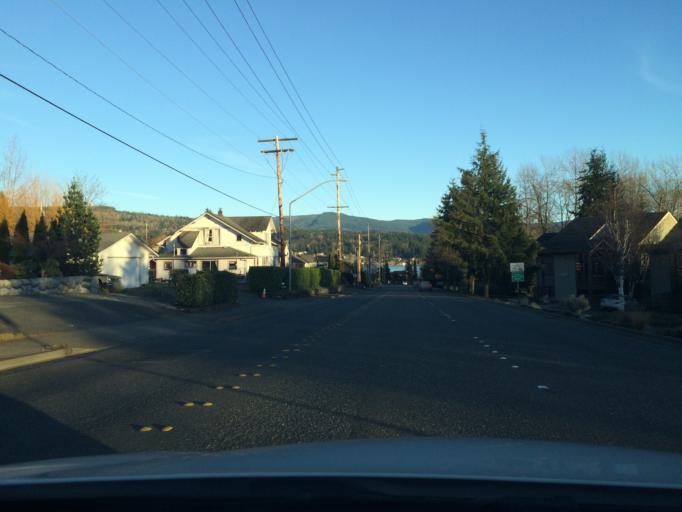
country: US
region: Washington
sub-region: Whatcom County
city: Geneva
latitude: 48.7630
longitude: -122.4242
